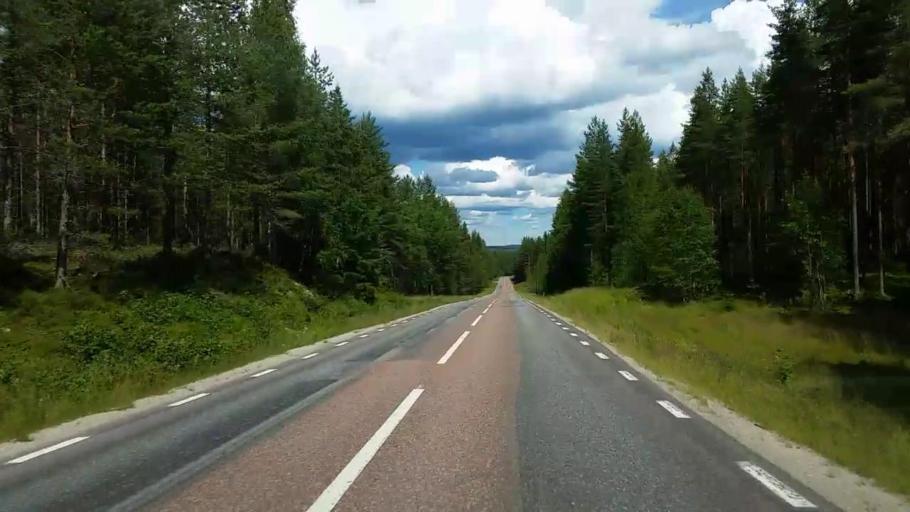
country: SE
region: Gaevleborg
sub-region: Ovanakers Kommun
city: Edsbyn
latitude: 61.3250
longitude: 15.5188
